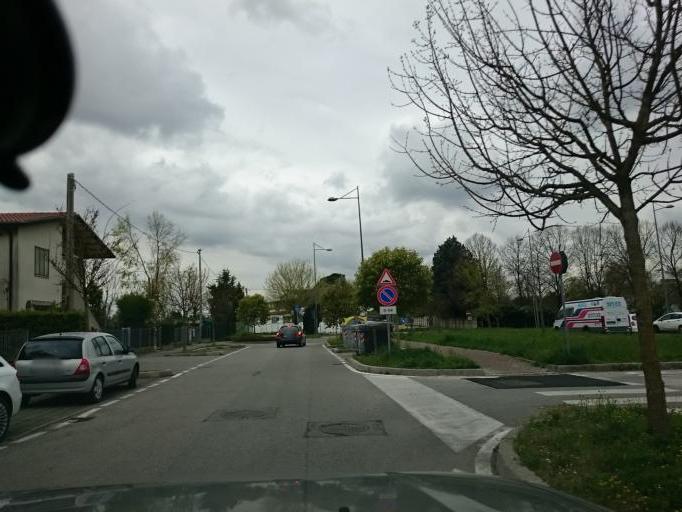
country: IT
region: Veneto
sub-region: Provincia di Padova
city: Padova
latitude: 45.3881
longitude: 11.9049
